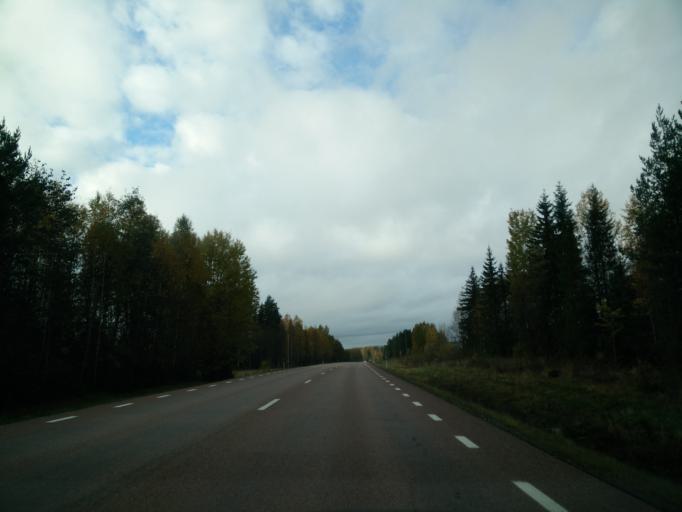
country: SE
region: Vaesternorrland
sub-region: Ange Kommun
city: Ange
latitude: 62.5174
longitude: 15.6013
